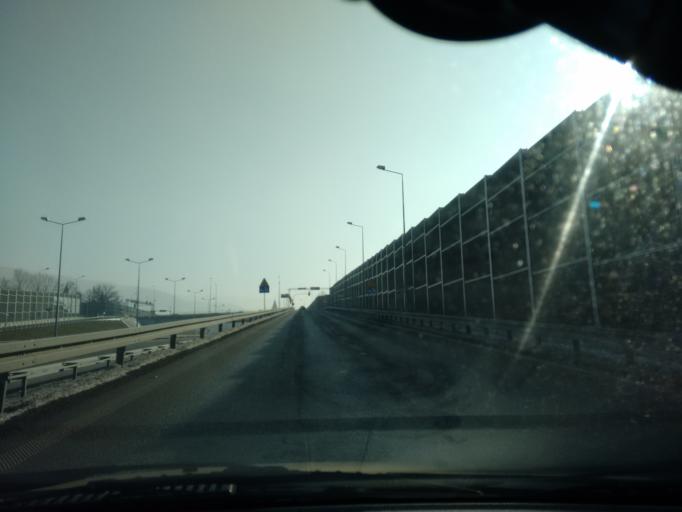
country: PL
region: Silesian Voivodeship
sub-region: Bielsko-Biala
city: Bielsko-Biala
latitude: 49.8251
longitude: 19.0855
